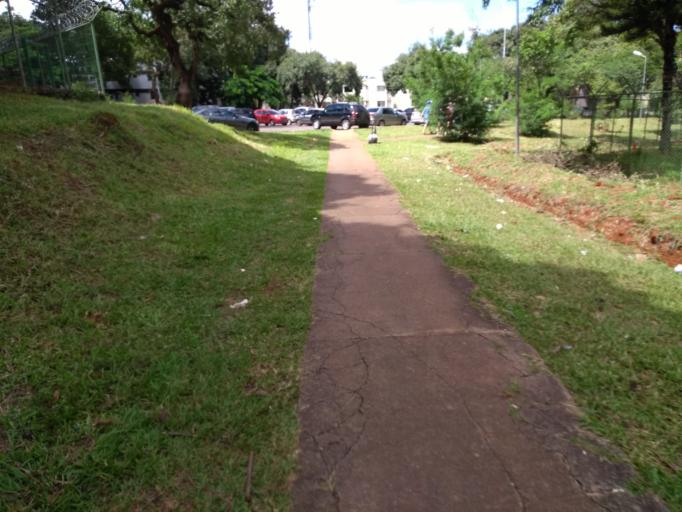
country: BR
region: Federal District
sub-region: Brasilia
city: Brasilia
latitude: -15.8087
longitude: -47.9430
